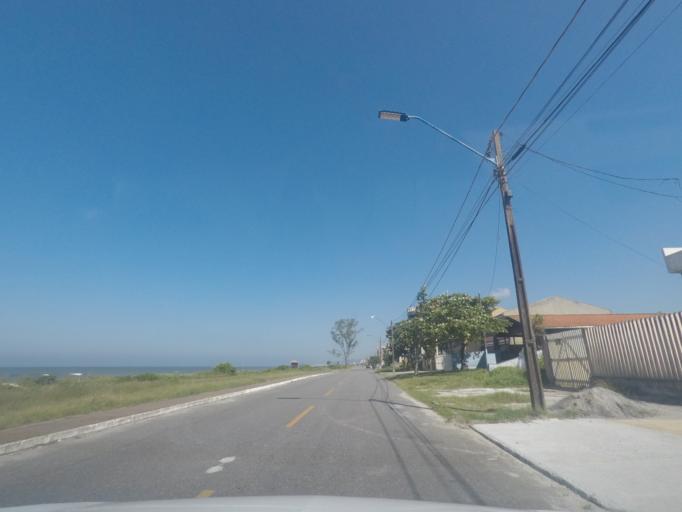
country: BR
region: Parana
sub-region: Pontal Do Parana
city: Pontal do Parana
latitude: -25.7546
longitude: -48.5029
